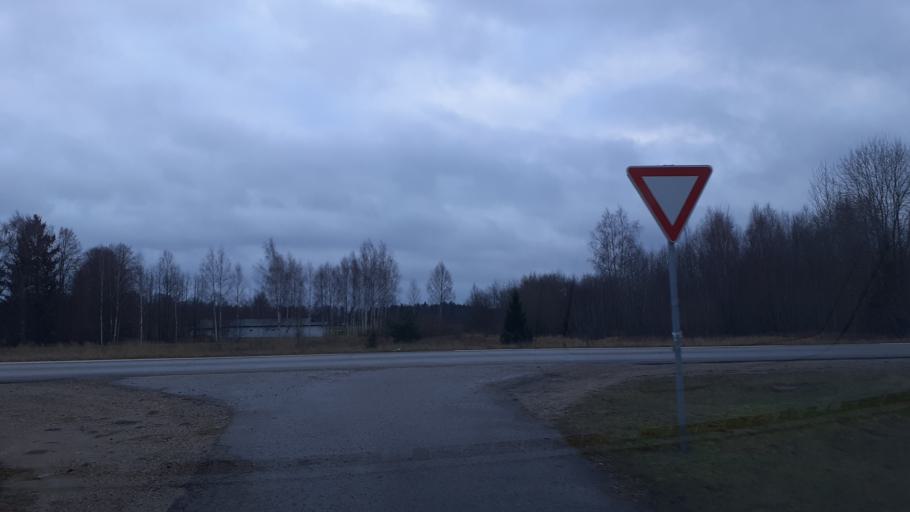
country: LV
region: Talsu Rajons
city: Stende
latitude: 57.0654
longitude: 22.2887
